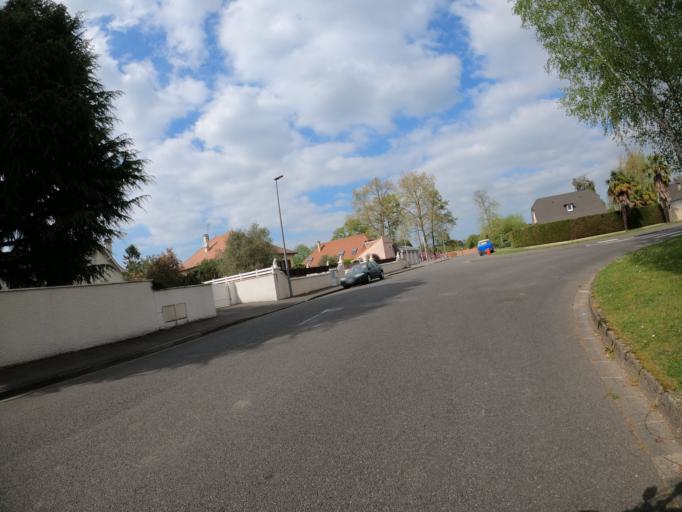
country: FR
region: Aquitaine
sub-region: Departement des Pyrenees-Atlantiques
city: Lons
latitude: 43.3259
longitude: -0.3893
